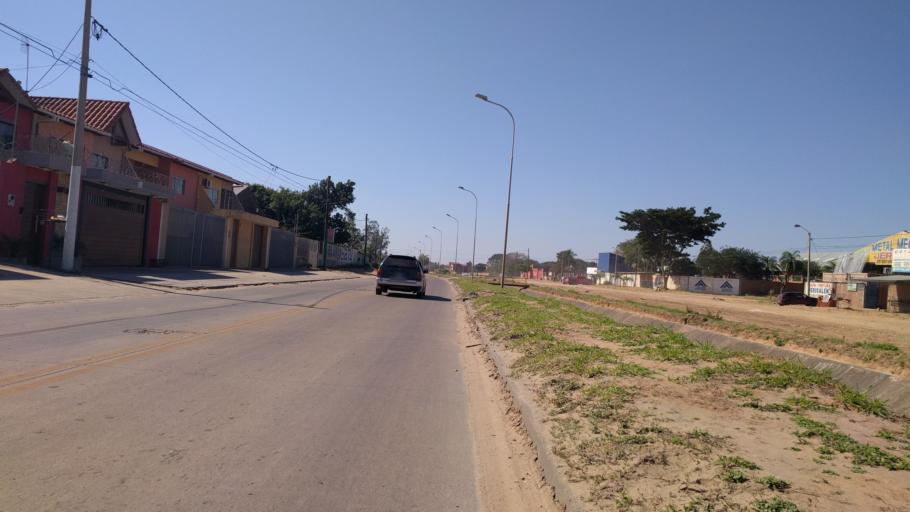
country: BO
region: Santa Cruz
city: Santa Cruz de la Sierra
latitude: -17.8424
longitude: -63.1920
